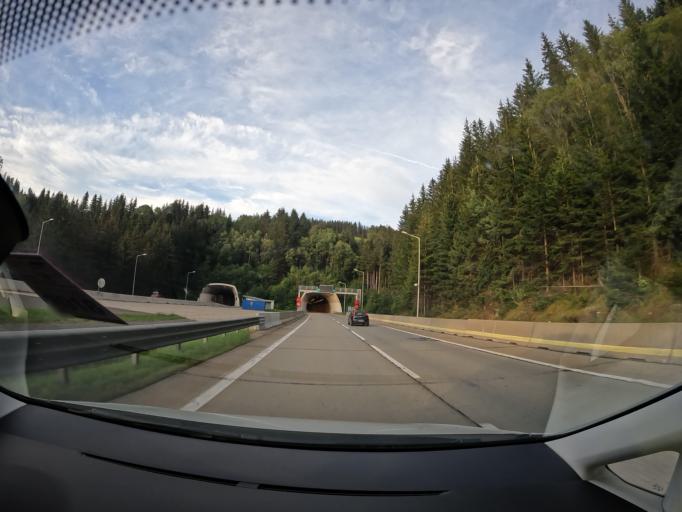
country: AT
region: Styria
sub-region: Politischer Bezirk Voitsberg
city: Pack
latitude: 46.9467
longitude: 15.0054
